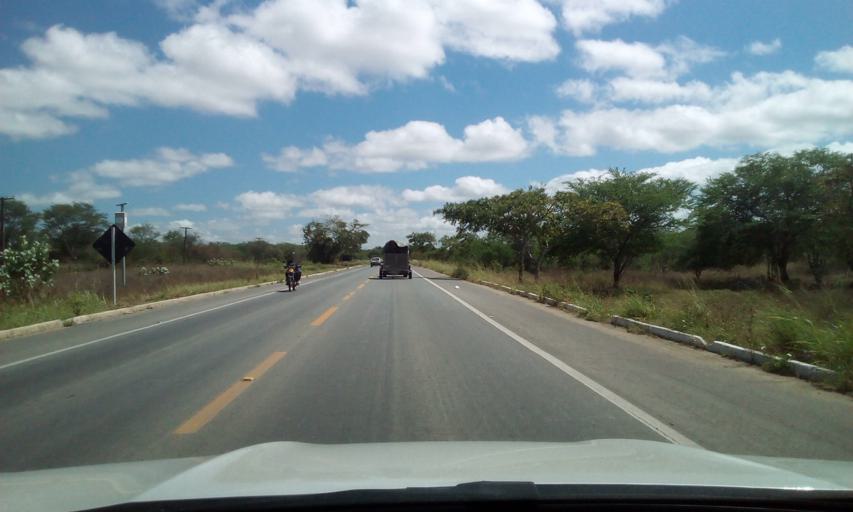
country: BR
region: Paraiba
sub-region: Campina Grande
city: Campina Grande
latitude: -7.3240
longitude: -35.8963
